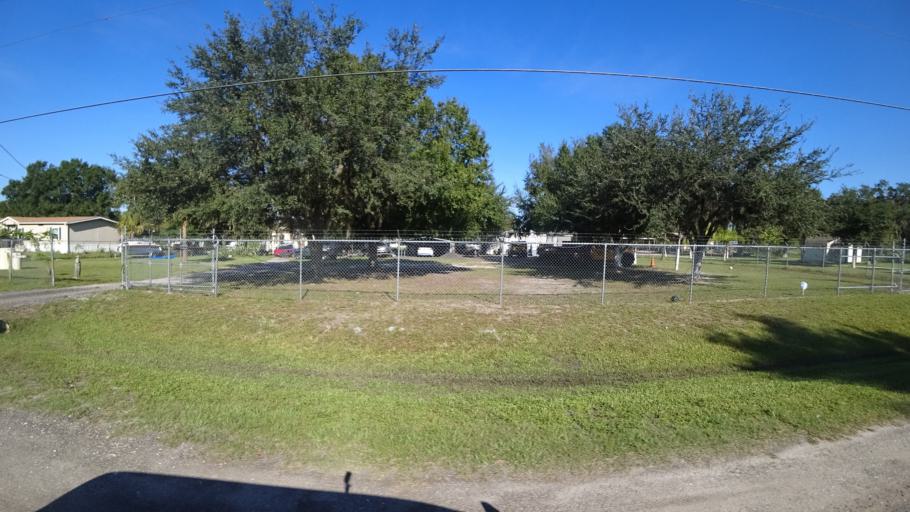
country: US
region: Florida
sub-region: Hillsborough County
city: Sun City Center
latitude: 27.6481
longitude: -82.3582
